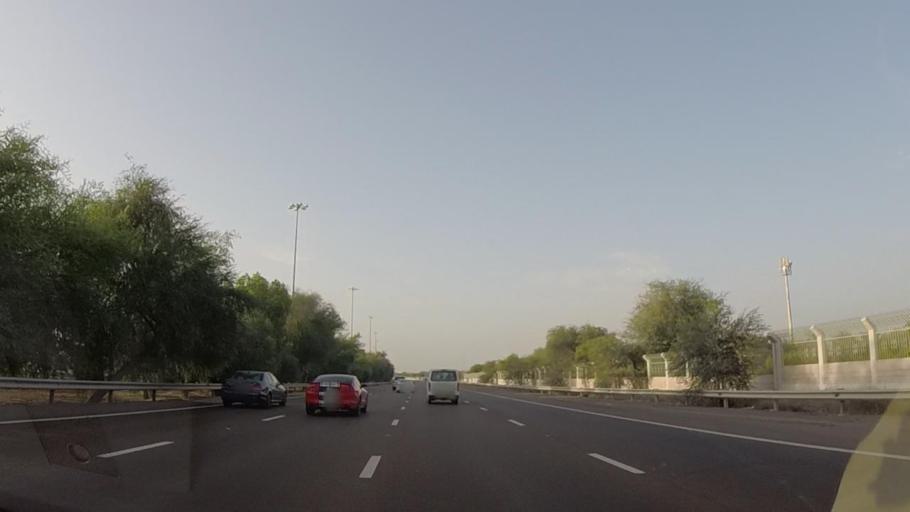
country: AE
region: Dubai
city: Dubai
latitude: 24.8165
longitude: 54.8728
